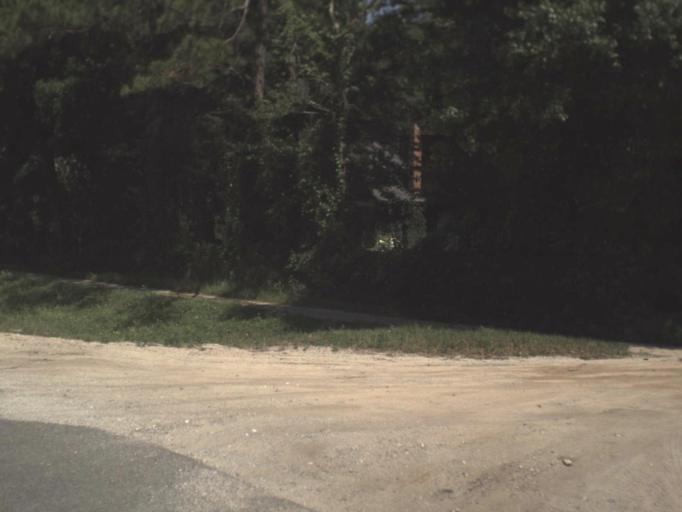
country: US
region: Florida
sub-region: Clay County
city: Green Cove Springs
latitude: 29.9839
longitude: -81.7143
